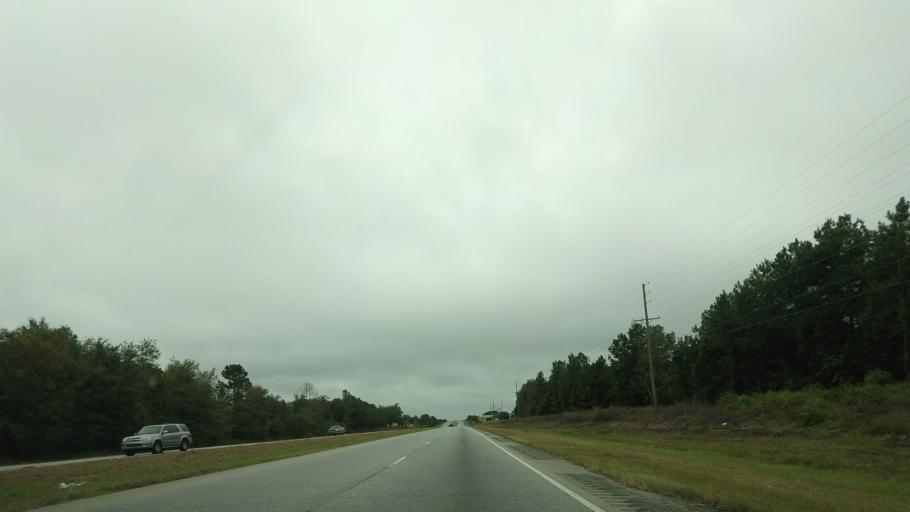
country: US
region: Georgia
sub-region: Lowndes County
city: Valdosta
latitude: 30.8387
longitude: -83.2280
